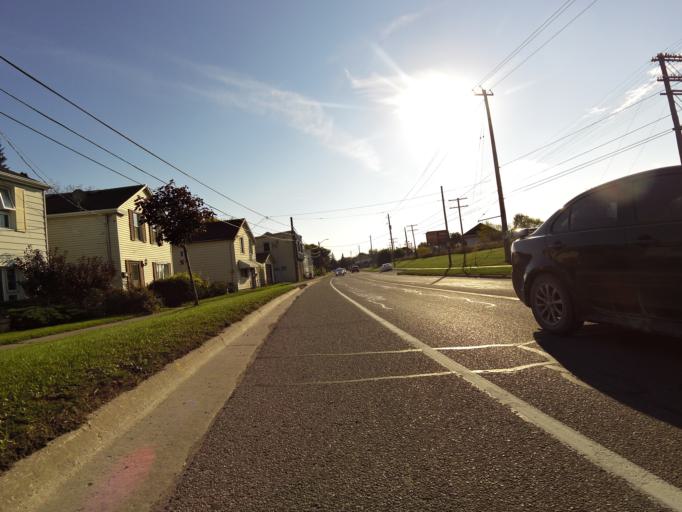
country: CA
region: Ontario
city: Kingston
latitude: 44.2545
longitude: -76.4834
